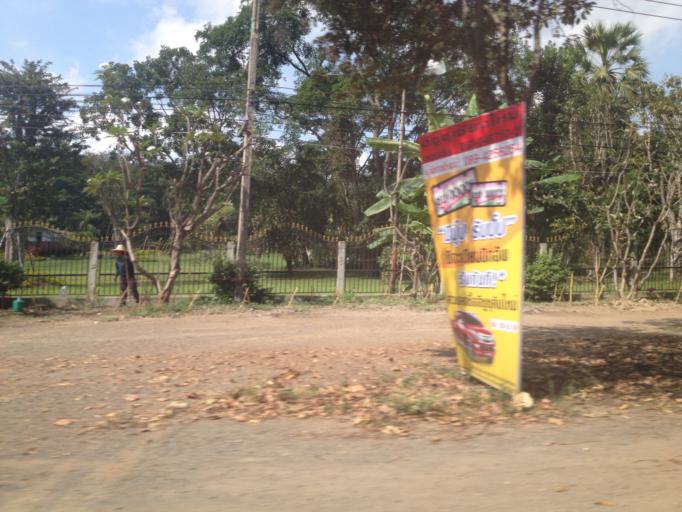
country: TH
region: Chiang Mai
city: Hang Dong
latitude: 18.7361
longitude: 98.8892
